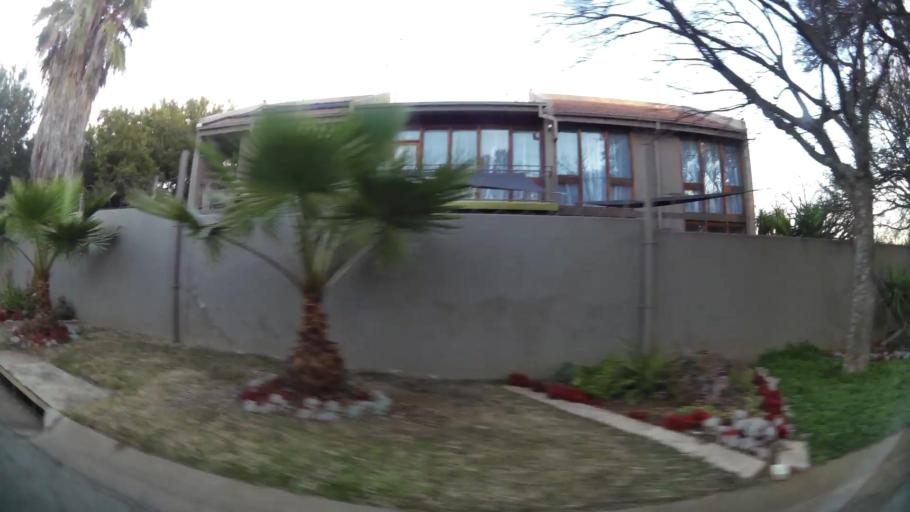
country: ZA
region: North-West
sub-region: Dr Kenneth Kaunda District Municipality
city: Potchefstroom
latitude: -26.7228
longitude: 27.1127
